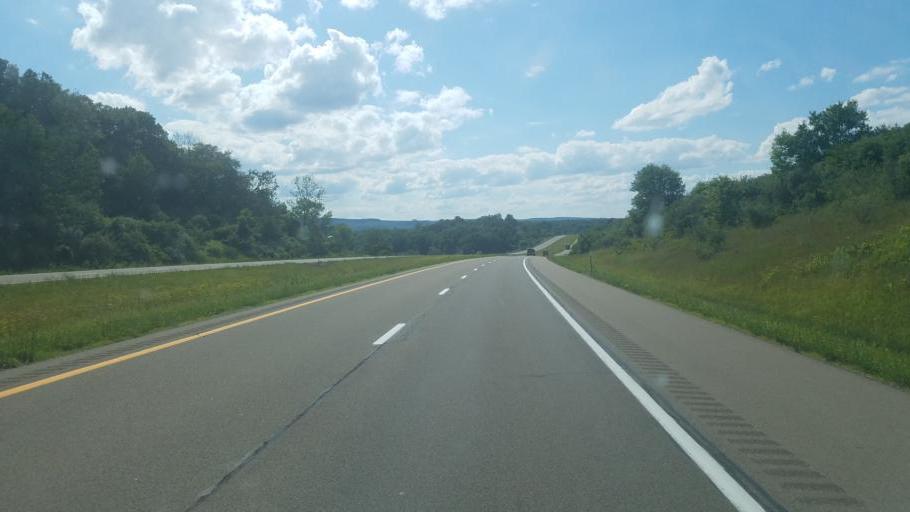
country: US
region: New York
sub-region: Steuben County
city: Hornell
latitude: 42.3754
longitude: -77.6411
